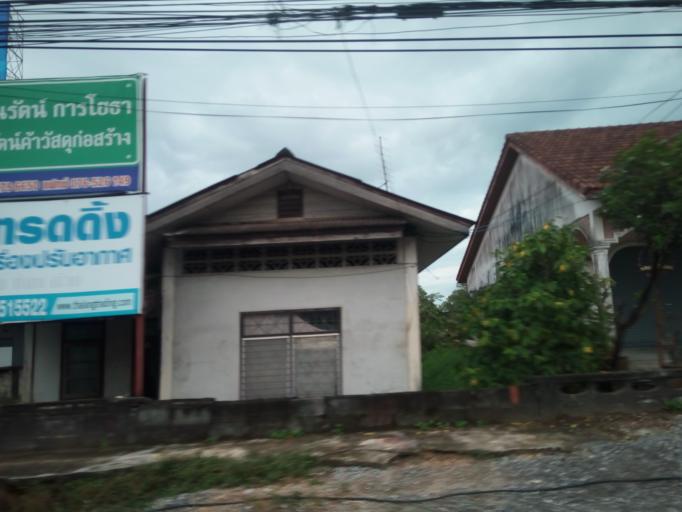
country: TH
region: Phuket
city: Thalang
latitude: 8.0929
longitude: 98.3387
